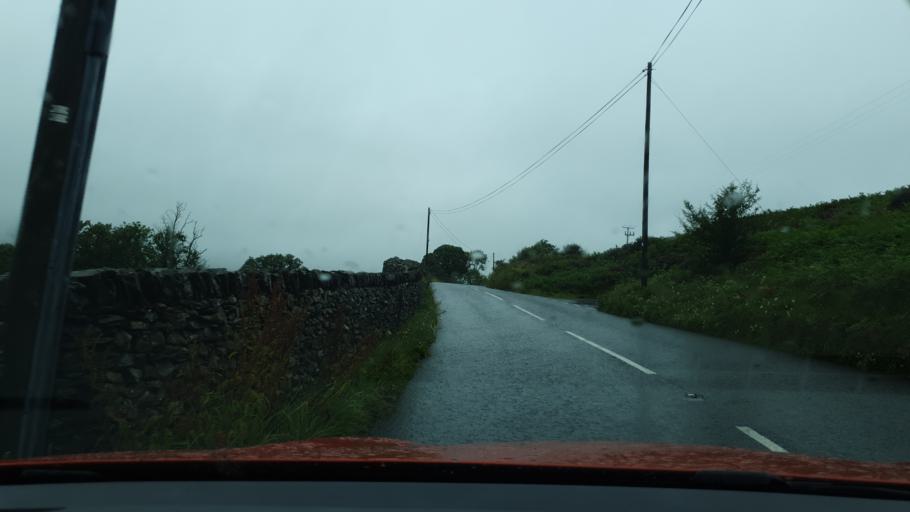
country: GB
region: England
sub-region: Cumbria
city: Ulverston
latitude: 54.3262
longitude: -3.0970
